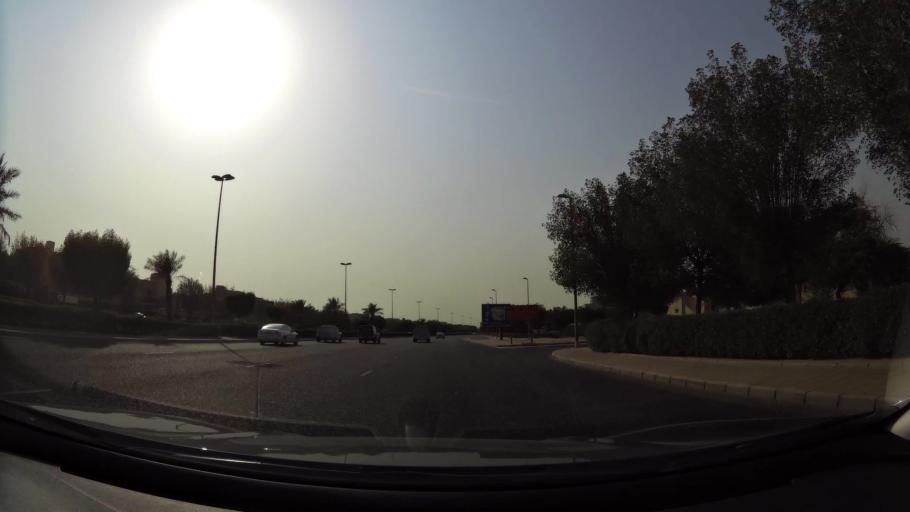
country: KW
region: Mubarak al Kabir
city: Mubarak al Kabir
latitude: 29.2090
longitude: 48.0884
